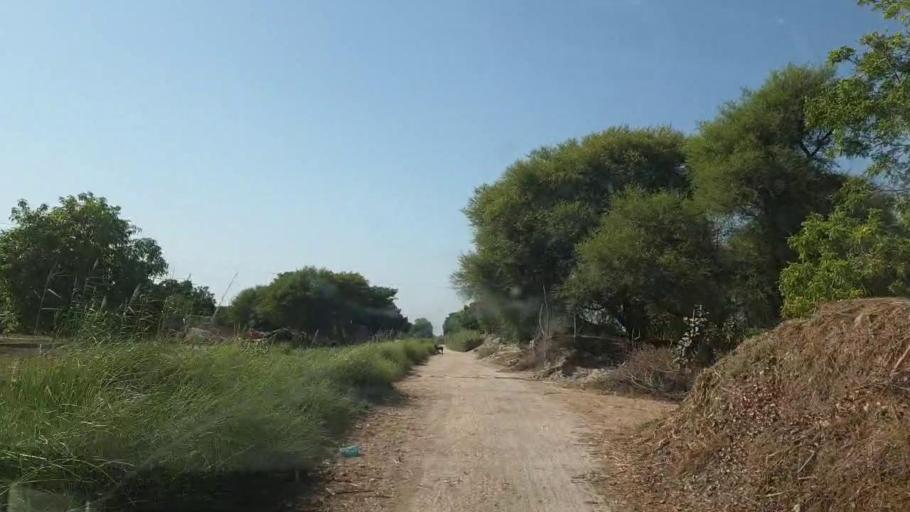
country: PK
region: Sindh
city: Tando Jam
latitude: 25.3120
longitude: 68.6103
